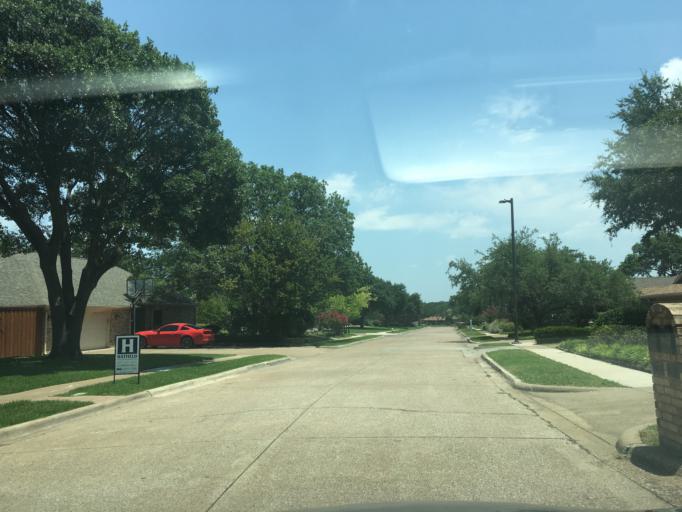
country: US
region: Texas
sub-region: Dallas County
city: Carrollton
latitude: 32.9478
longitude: -96.8682
